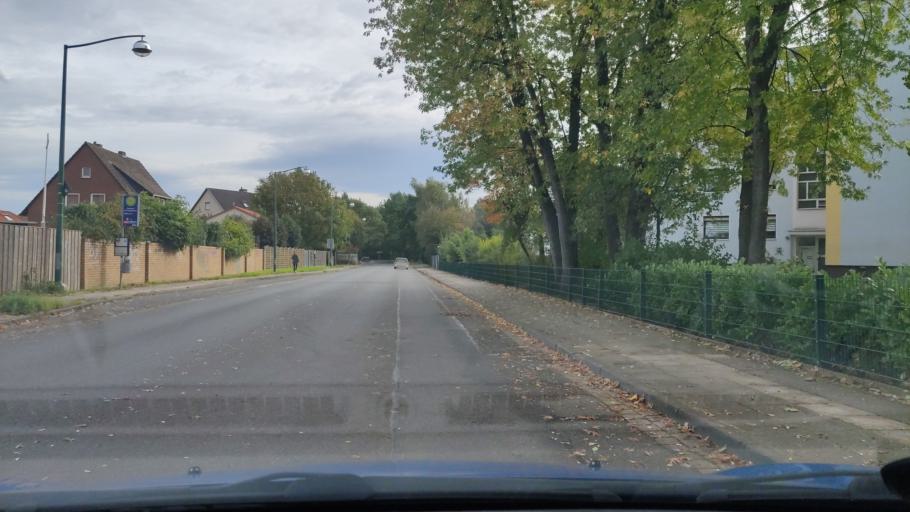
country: DE
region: Lower Saxony
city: Langenhagen
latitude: 52.4335
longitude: 9.7073
